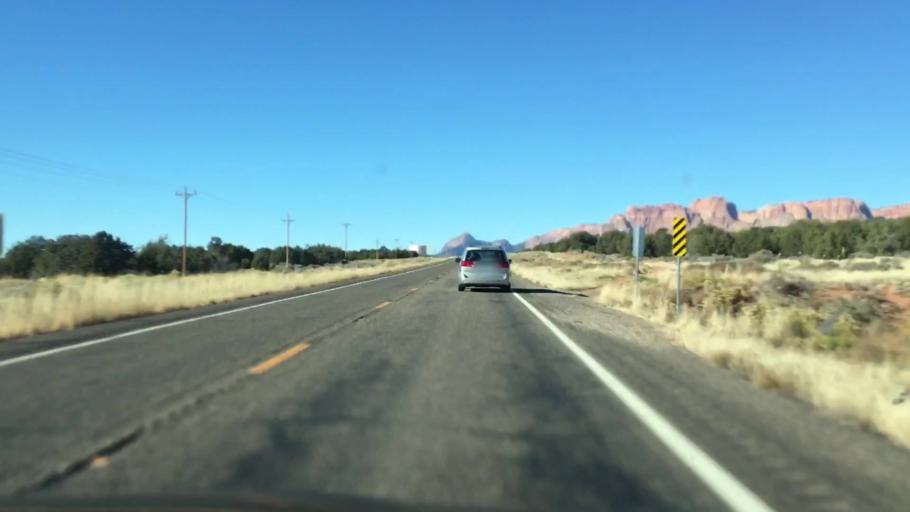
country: US
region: Arizona
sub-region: Mohave County
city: Colorado City
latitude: 36.9541
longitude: -112.9615
